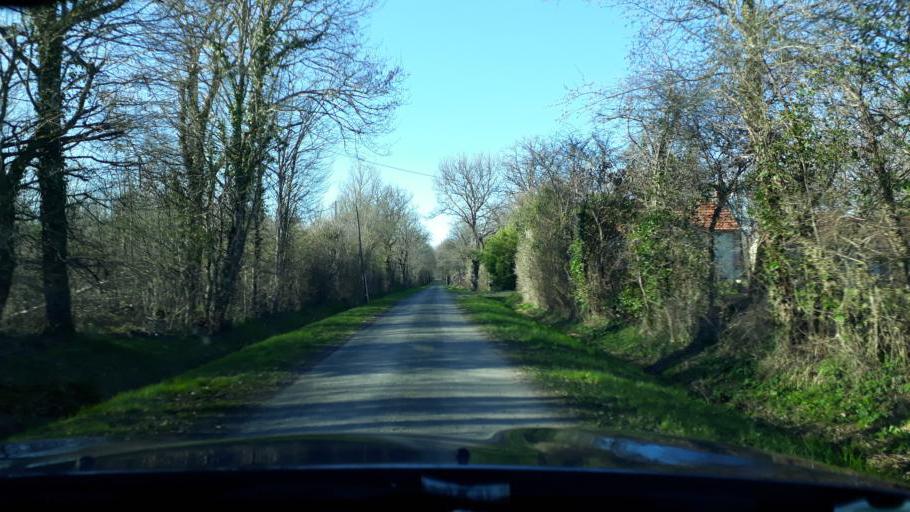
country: FR
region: Centre
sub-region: Departement du Loiret
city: Jouy-le-Potier
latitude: 47.7082
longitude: 1.8343
